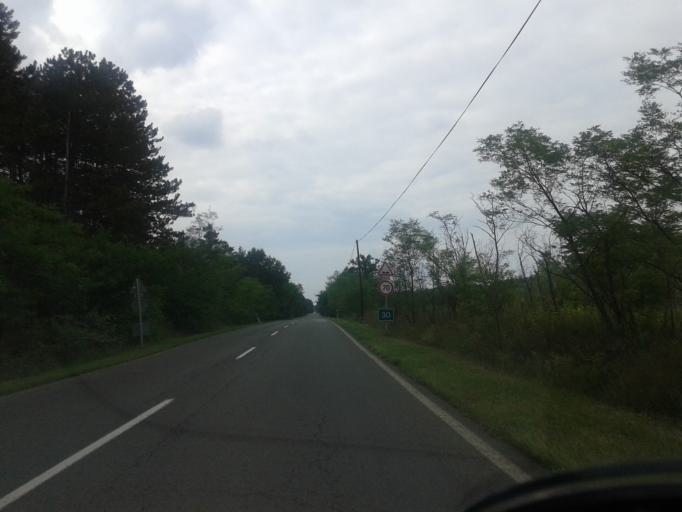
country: HU
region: Csongrad
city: Asotthalom
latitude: 46.2170
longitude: 19.7799
